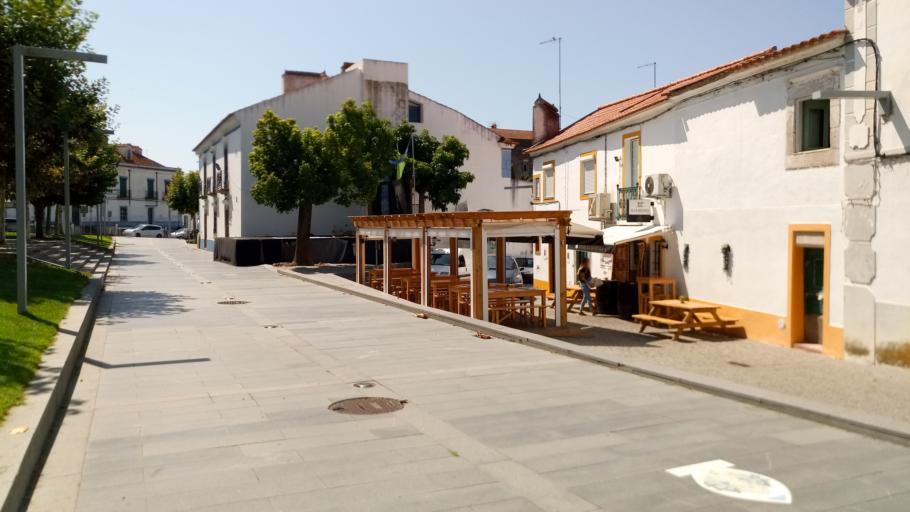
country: PT
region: Evora
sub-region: Arraiolos
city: Arraiolos
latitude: 38.7238
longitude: -7.9844
